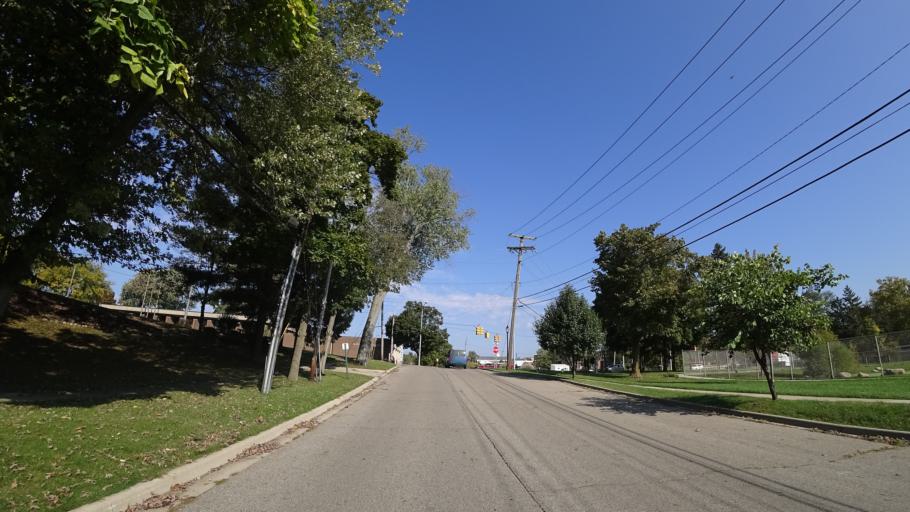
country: US
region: Michigan
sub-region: Saint Joseph County
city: Three Rivers
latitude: 41.9423
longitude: -85.6358
